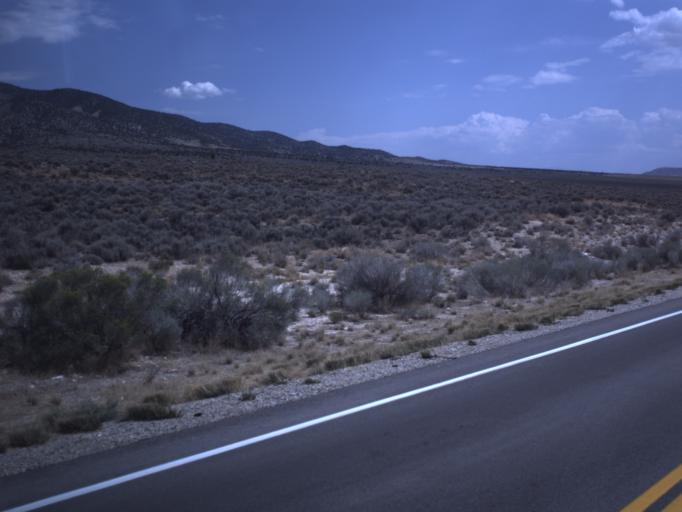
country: US
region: Utah
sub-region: Tooele County
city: Tooele
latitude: 40.2914
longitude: -112.2713
